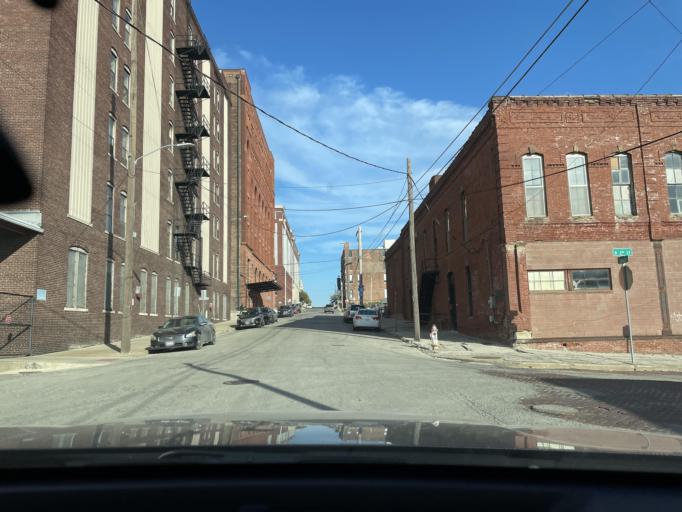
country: US
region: Missouri
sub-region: Buchanan County
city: Saint Joseph
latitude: 39.7682
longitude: -94.8582
